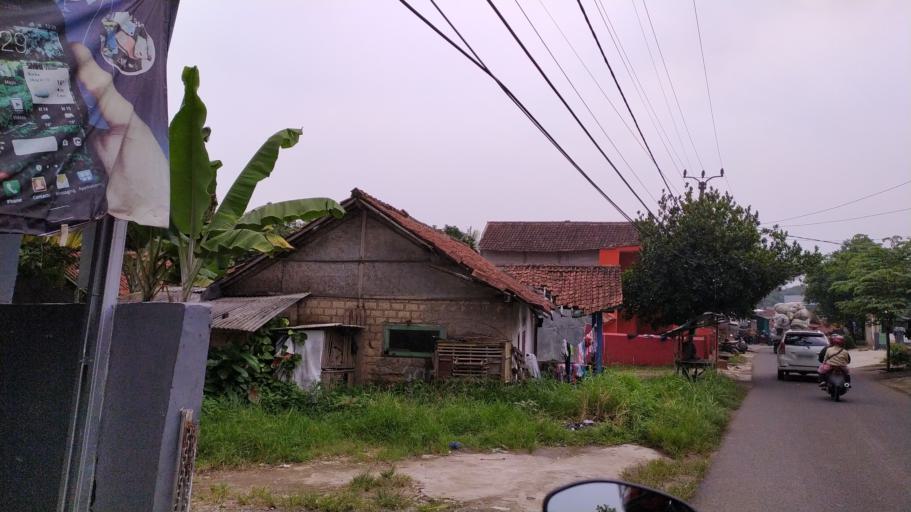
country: ID
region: West Java
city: Ciampea
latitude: -6.5948
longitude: 106.7049
